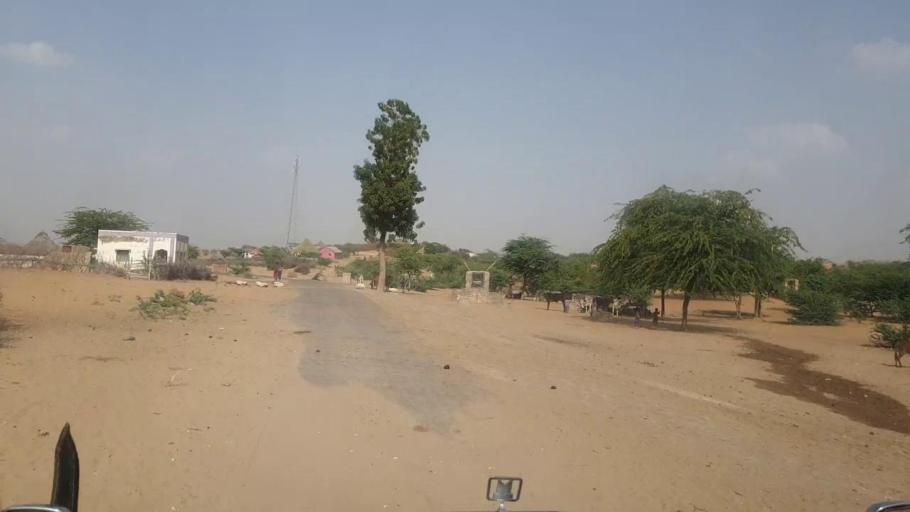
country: PK
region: Sindh
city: Islamkot
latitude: 25.2178
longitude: 70.2880
